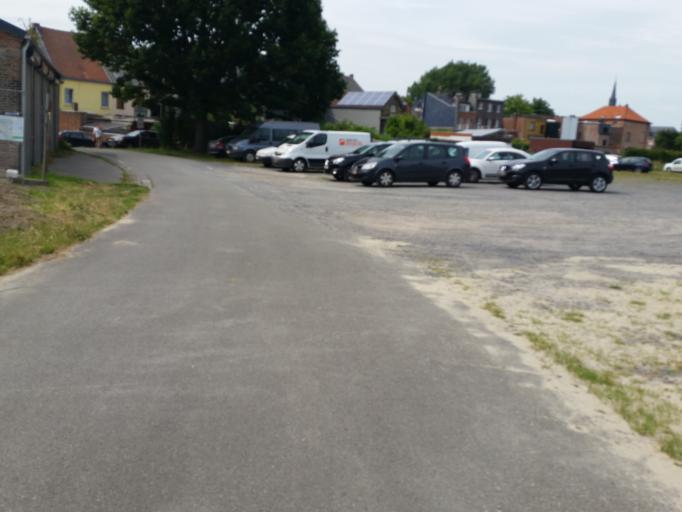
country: BE
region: Flanders
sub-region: Provincie Antwerpen
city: Boom
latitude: 51.0798
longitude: 4.3685
